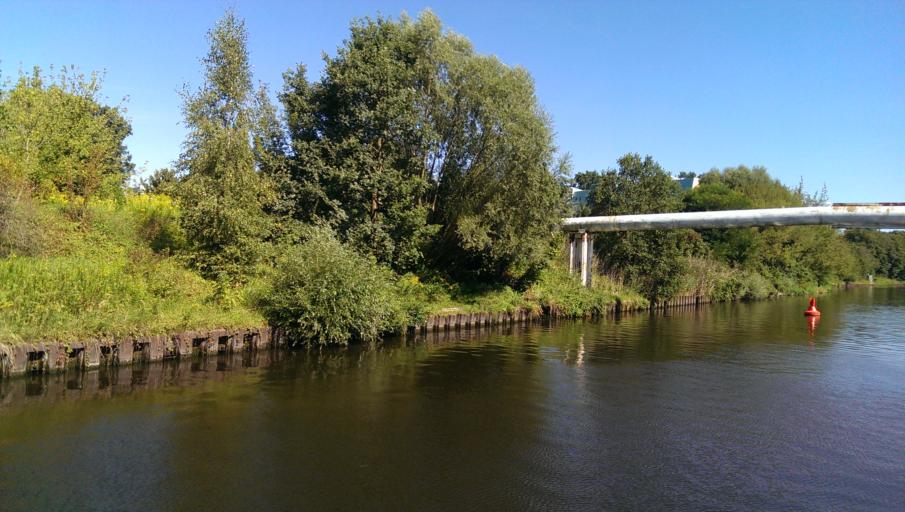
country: DE
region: Brandenburg
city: Teltow
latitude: 52.4043
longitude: 13.2480
